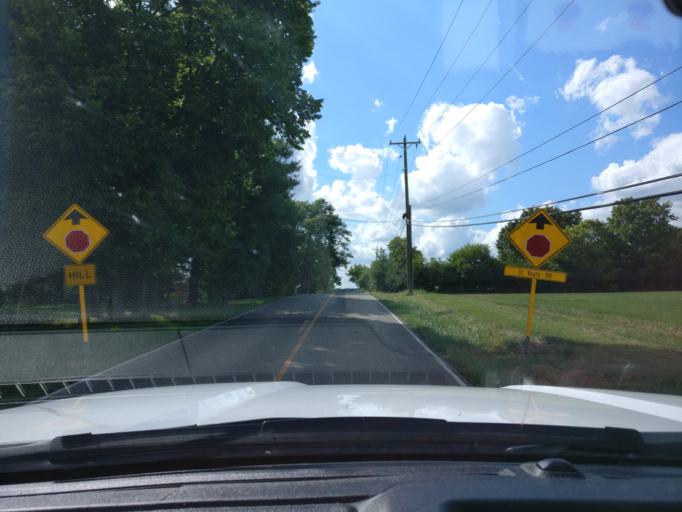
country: US
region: Ohio
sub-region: Warren County
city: Springboro
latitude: 39.5075
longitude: -84.2371
